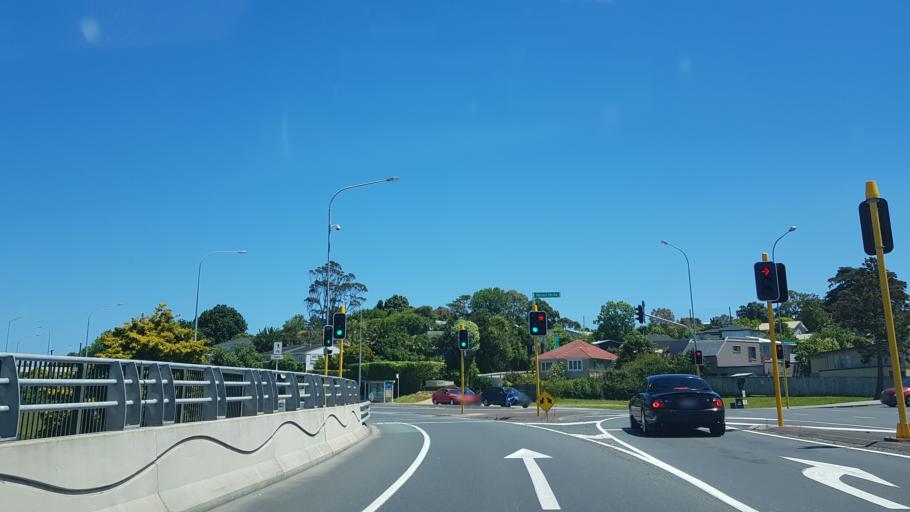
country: NZ
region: Auckland
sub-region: Auckland
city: North Shore
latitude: -36.7805
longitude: 174.7502
